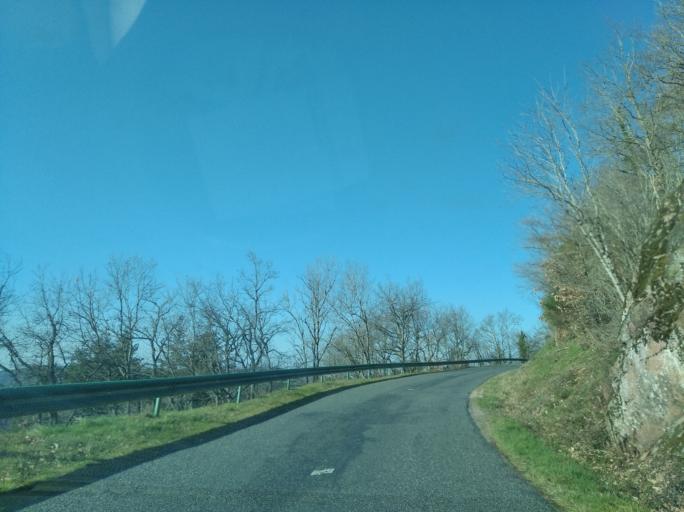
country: FR
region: Auvergne
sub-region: Departement de l'Allier
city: Le Mayet-de-Montagne
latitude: 46.1077
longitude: 3.6801
